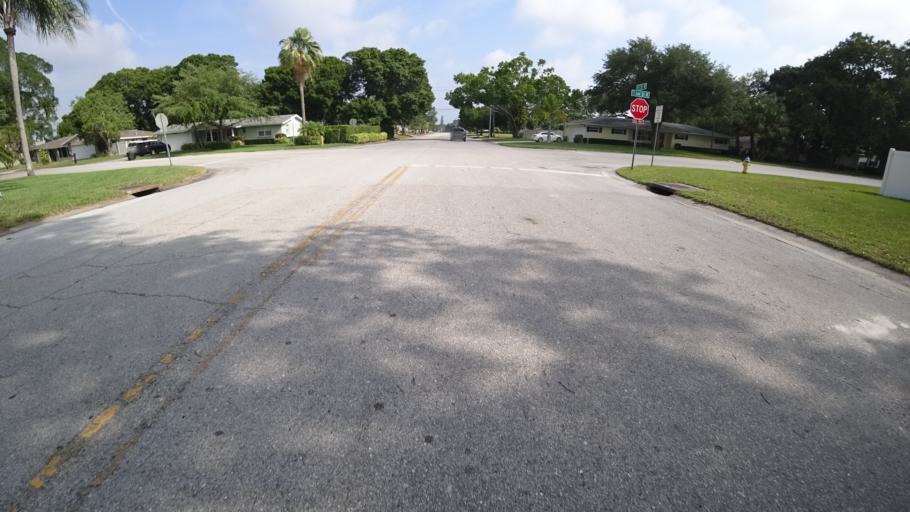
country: US
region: Florida
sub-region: Manatee County
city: West Bradenton
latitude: 27.4934
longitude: -82.6162
